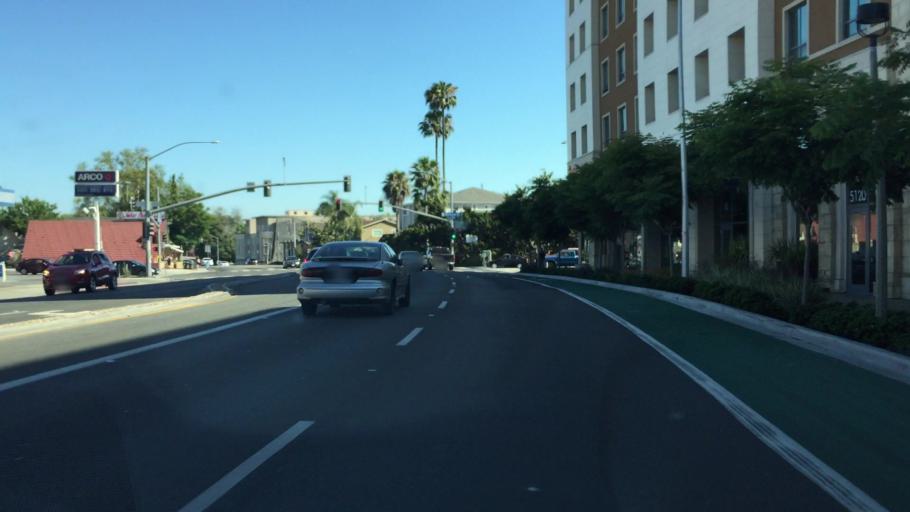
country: US
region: California
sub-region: San Diego County
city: La Mesa
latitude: 32.7714
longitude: -117.0701
